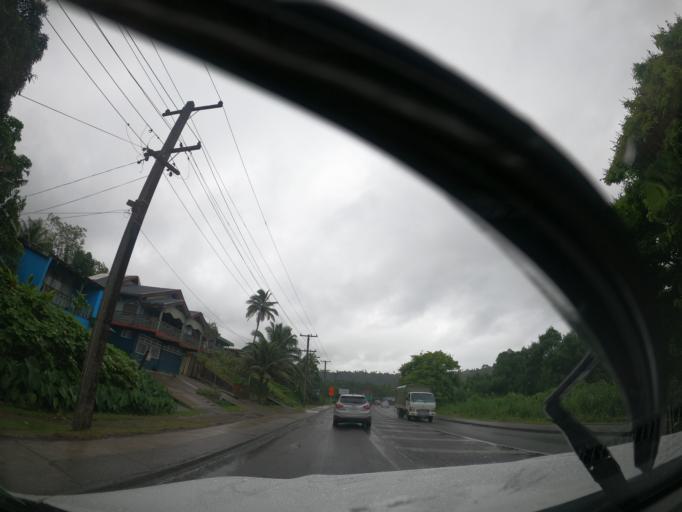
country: FJ
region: Central
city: Suva
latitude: -18.1131
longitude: 178.4285
